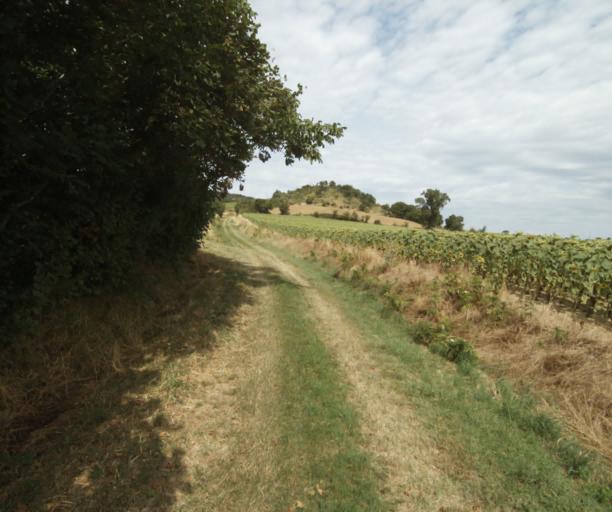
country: FR
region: Midi-Pyrenees
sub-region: Departement de la Haute-Garonne
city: Saint-Felix-Lauragais
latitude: 43.4438
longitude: 1.9055
